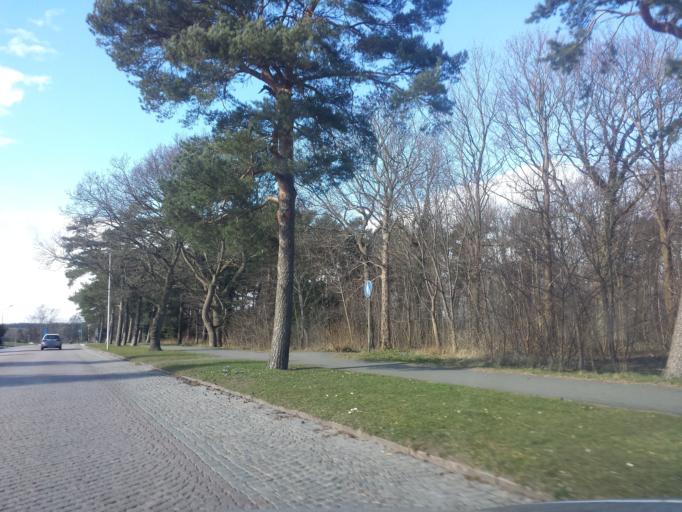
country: SE
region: Skane
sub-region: Simrishamns Kommun
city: Simrishamn
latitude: 55.5613
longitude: 14.3401
